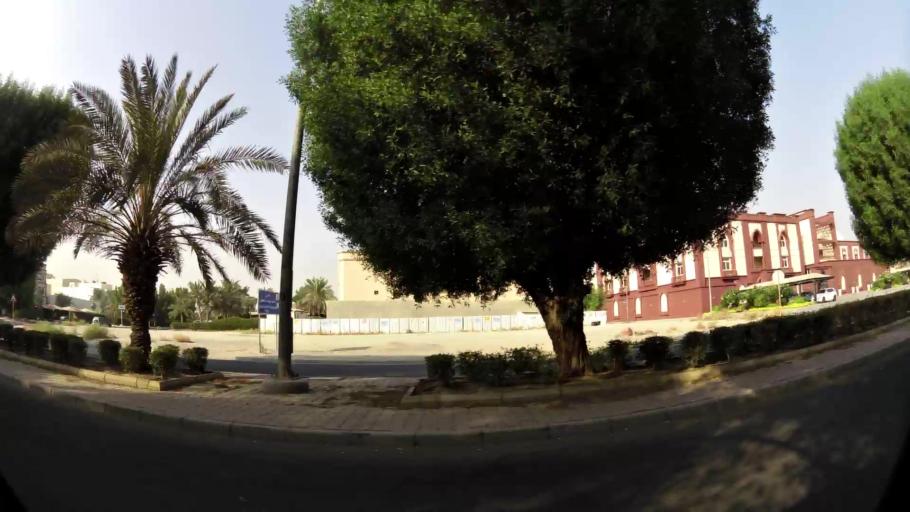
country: KW
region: Muhafazat Hawalli
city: Salwa
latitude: 29.2762
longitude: 48.0798
